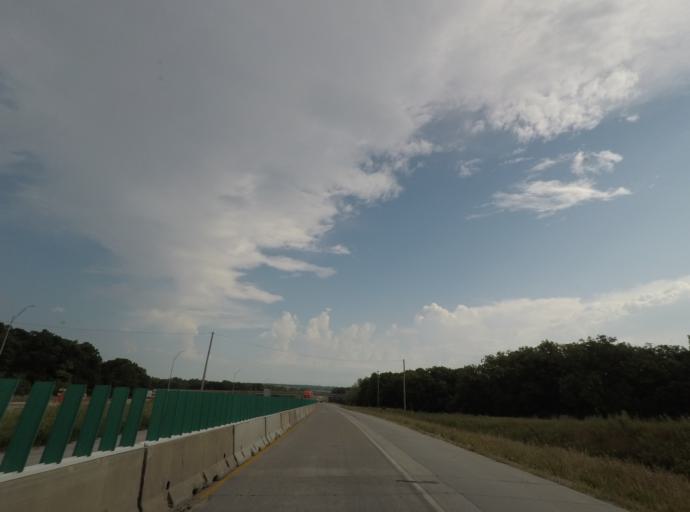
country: US
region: Iowa
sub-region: Decatur County
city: Lamoni
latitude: 40.6540
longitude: -93.8585
